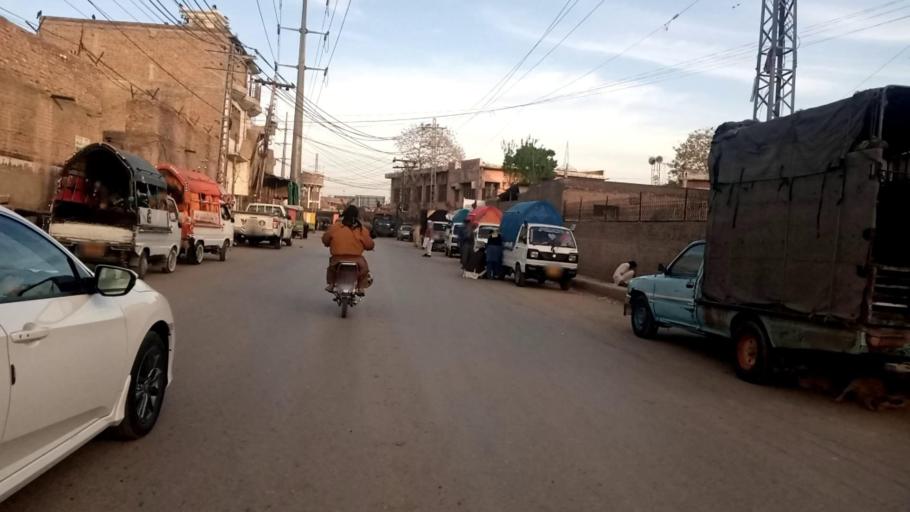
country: PK
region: Khyber Pakhtunkhwa
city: Peshawar
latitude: 34.0192
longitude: 71.5676
